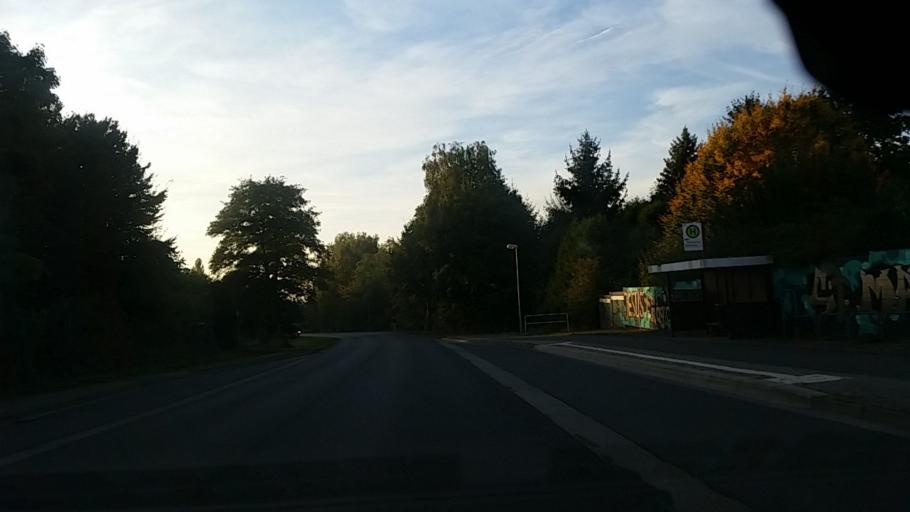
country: DE
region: Lower Saxony
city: Wolfsburg
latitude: 52.4202
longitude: 10.8407
